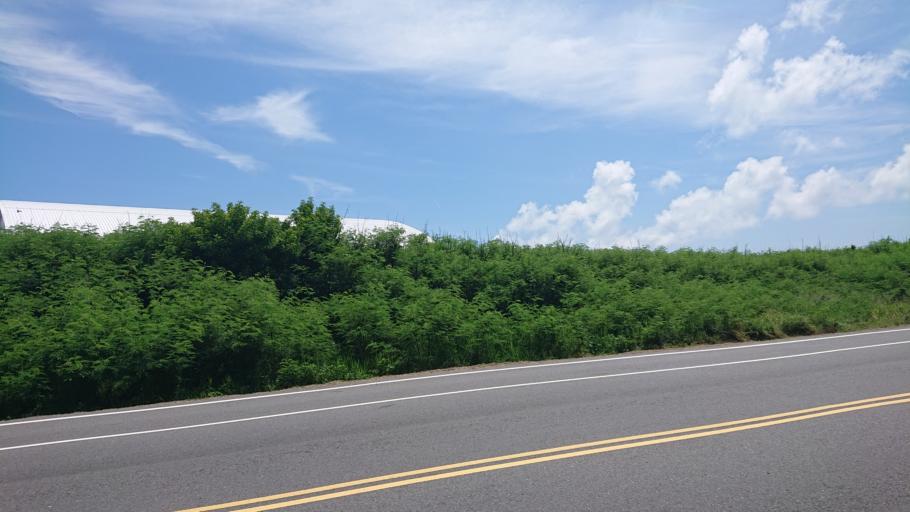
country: TW
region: Taiwan
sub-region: Penghu
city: Ma-kung
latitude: 23.6448
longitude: 119.5958
